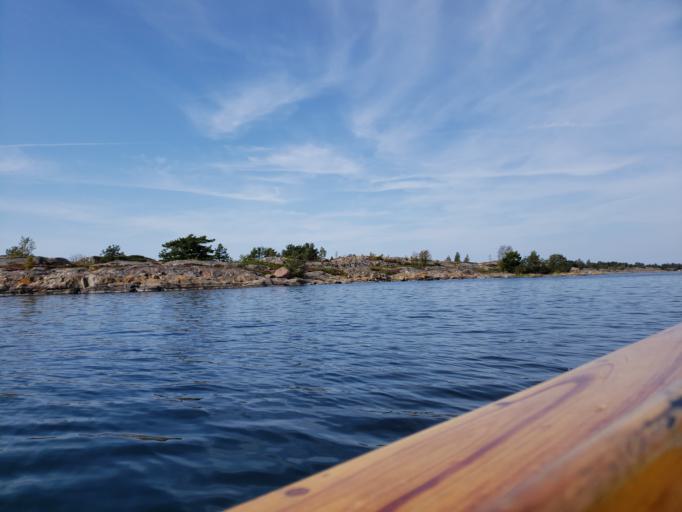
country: FI
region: Varsinais-Suomi
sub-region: Aboland-Turunmaa
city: Dragsfjaerd
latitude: 59.8429
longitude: 22.2053
